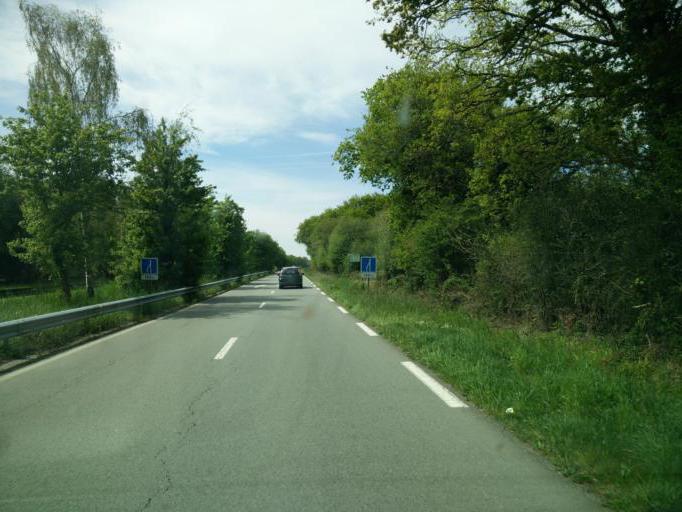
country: FR
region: Brittany
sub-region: Departement d'Ille-et-Vilaine
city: Dinard
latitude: 48.6064
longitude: -2.0755
